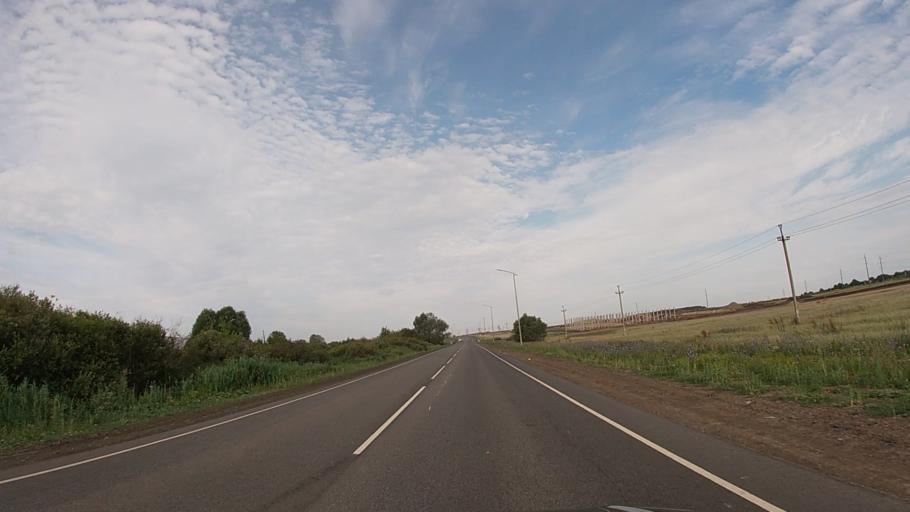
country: RU
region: Belgorod
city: Severnyy
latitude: 50.6674
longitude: 36.5499
